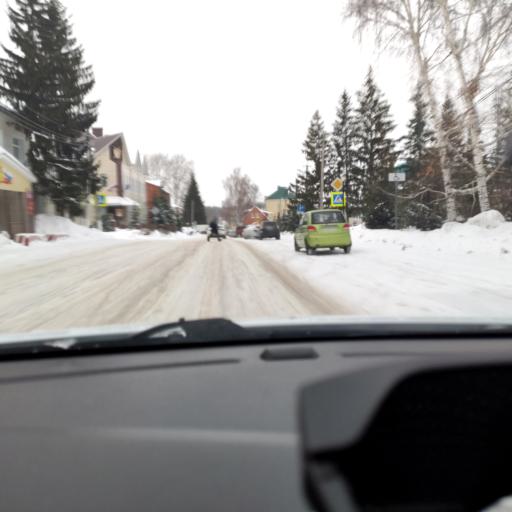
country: RU
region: Tatarstan
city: Vysokaya Gora
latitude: 55.9332
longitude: 49.3044
